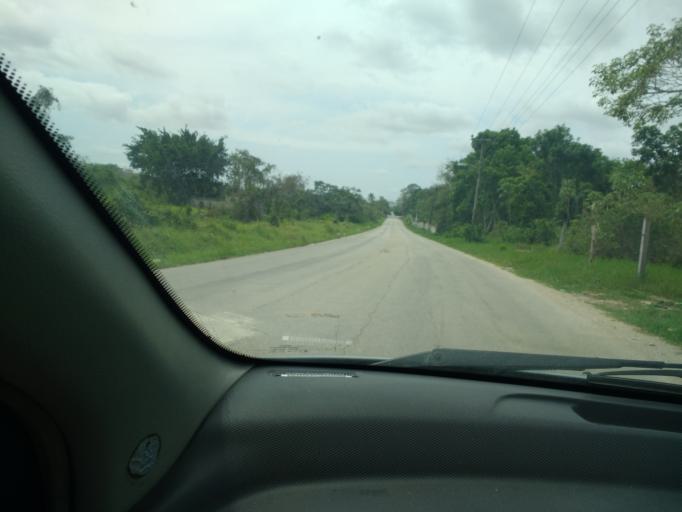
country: GT
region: Peten
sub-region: Municipio de San Benito
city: San Benito
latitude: 16.9176
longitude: -89.9290
